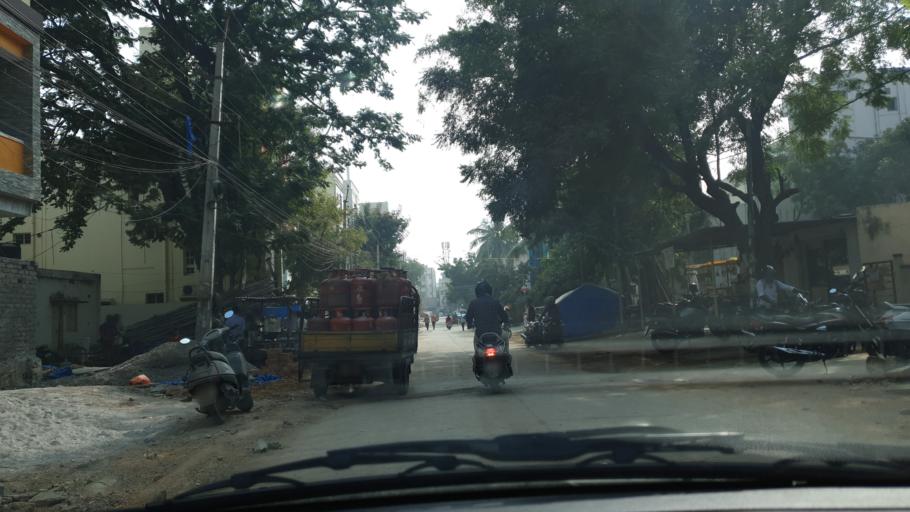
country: IN
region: Telangana
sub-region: Rangareddi
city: Kukatpalli
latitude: 17.4847
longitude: 78.4063
